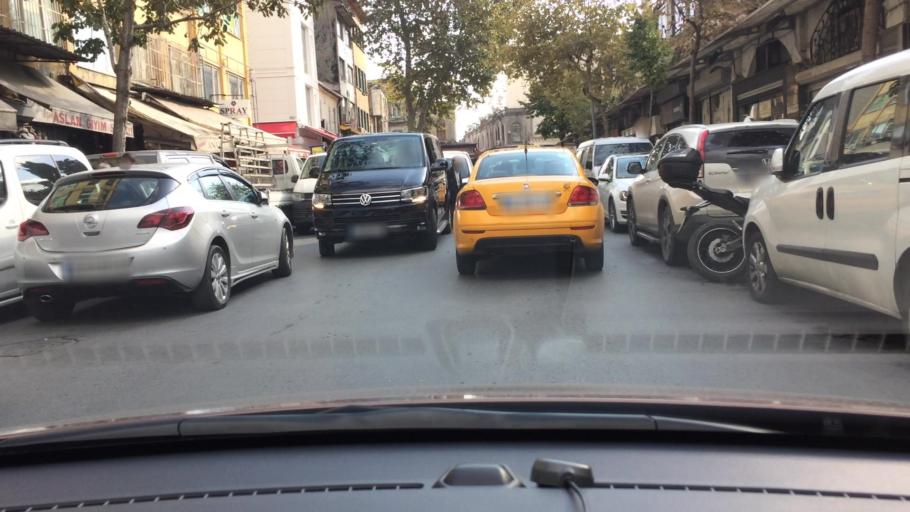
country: TR
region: Istanbul
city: Eminoenue
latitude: 41.0123
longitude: 28.9661
